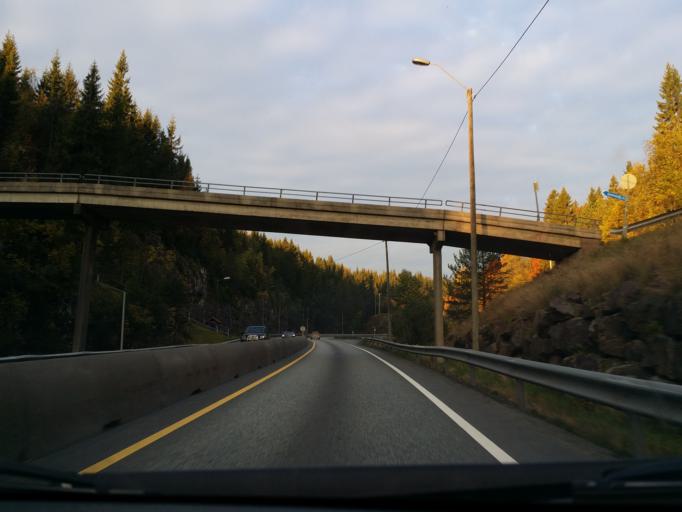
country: NO
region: Akershus
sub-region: Baerum
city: Skui
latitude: 59.9469
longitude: 10.3955
